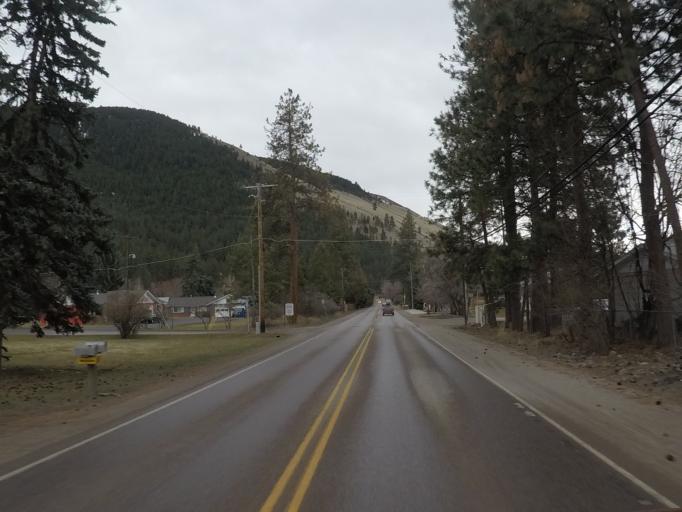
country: US
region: Montana
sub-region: Missoula County
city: East Missoula
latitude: 46.8893
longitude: -113.9657
